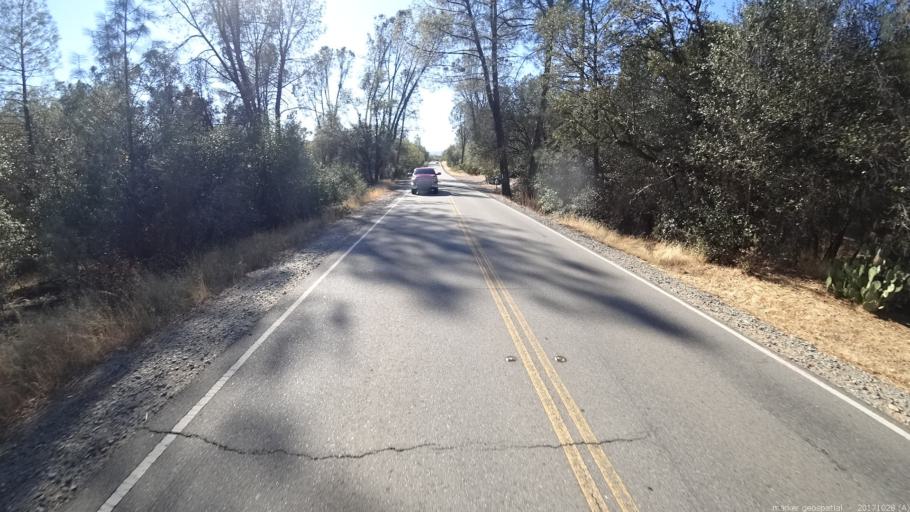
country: US
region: California
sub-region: Shasta County
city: Redding
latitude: 40.6234
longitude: -122.4204
